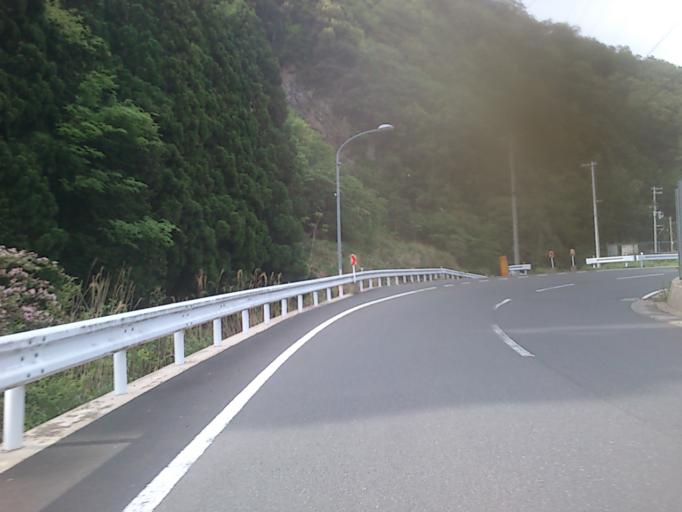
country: JP
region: Kyoto
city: Miyazu
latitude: 35.6380
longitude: 135.0135
